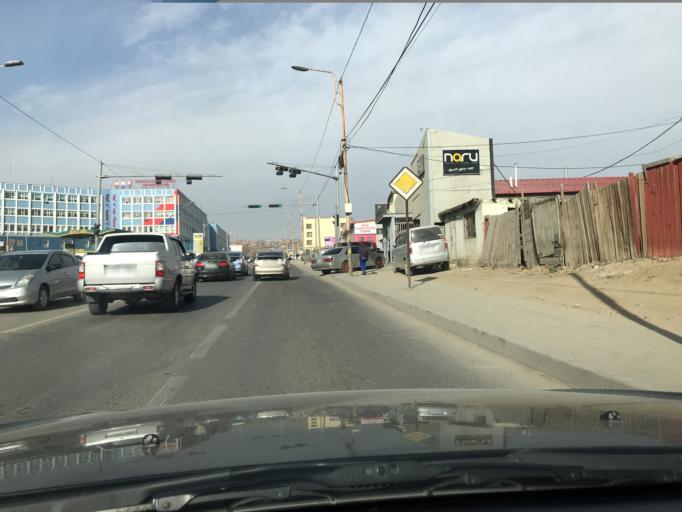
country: MN
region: Ulaanbaatar
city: Ulaanbaatar
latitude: 47.9278
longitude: 106.8924
